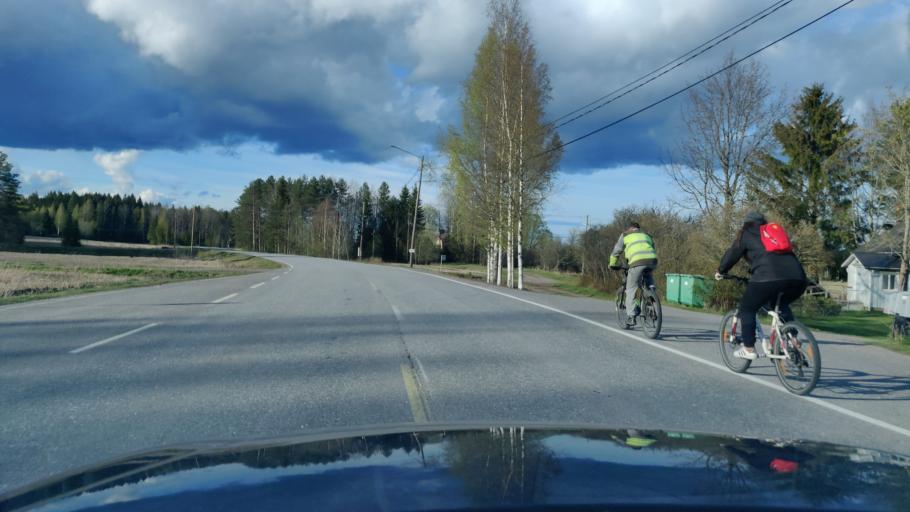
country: FI
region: Uusimaa
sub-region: Helsinki
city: Tuusula
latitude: 60.4579
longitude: 24.9846
